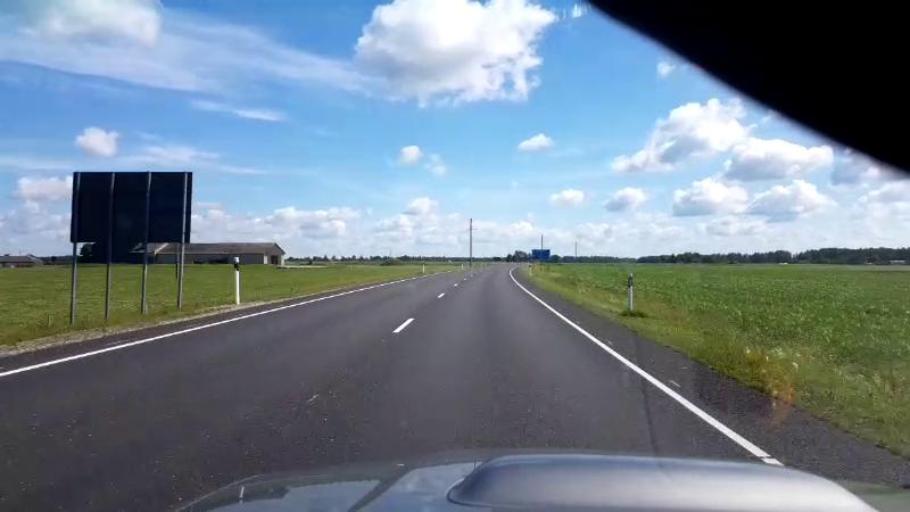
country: EE
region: Jaervamaa
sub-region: Jaerva-Jaani vald
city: Jarva-Jaani
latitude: 59.1372
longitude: 25.7622
